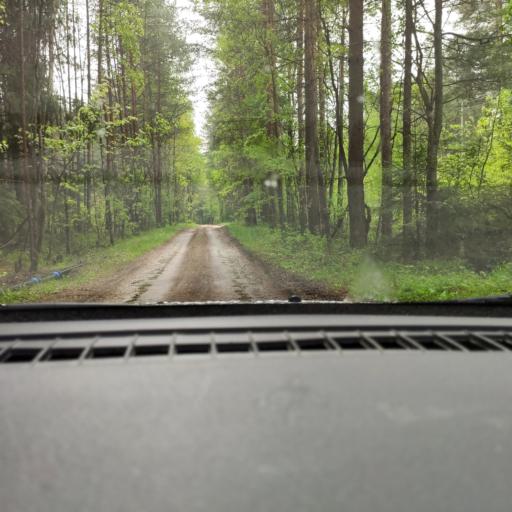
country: RU
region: Perm
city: Overyata
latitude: 58.0160
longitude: 55.8775
